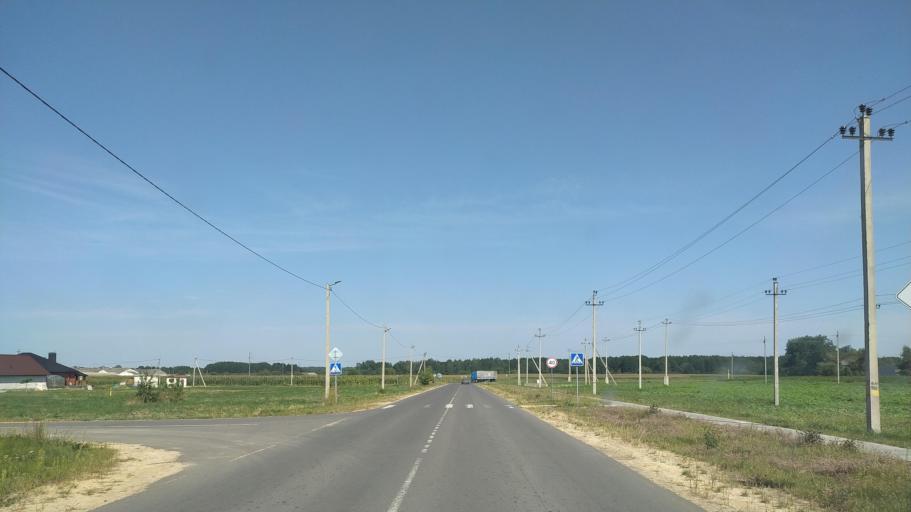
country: BY
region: Brest
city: Byaroza
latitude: 52.5204
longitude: 24.9866
